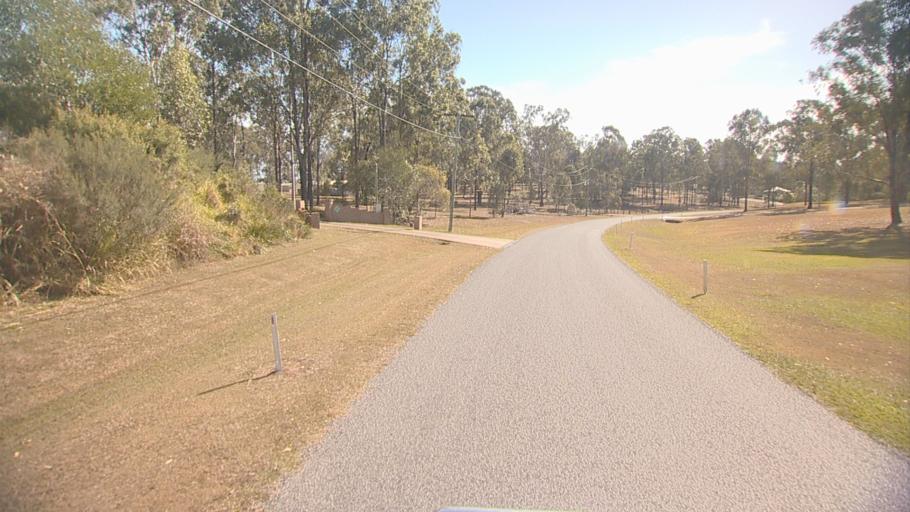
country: AU
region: Queensland
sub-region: Logan
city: Cedar Vale
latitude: -27.8729
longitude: 152.9775
